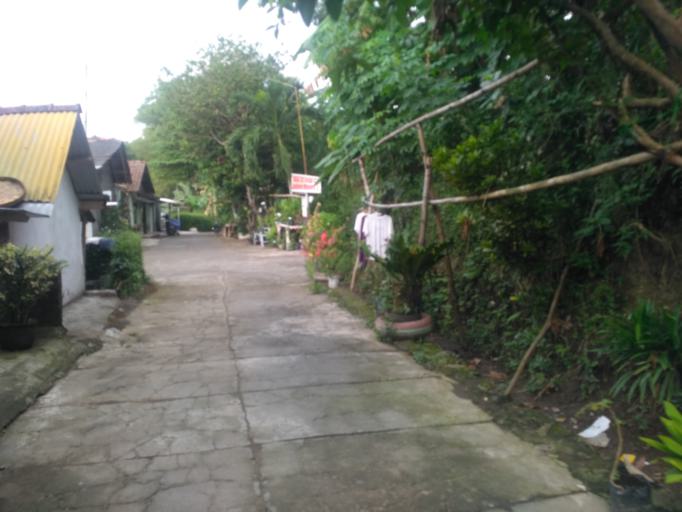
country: ID
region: Daerah Istimewa Yogyakarta
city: Yogyakarta
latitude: -7.7647
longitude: 110.3525
